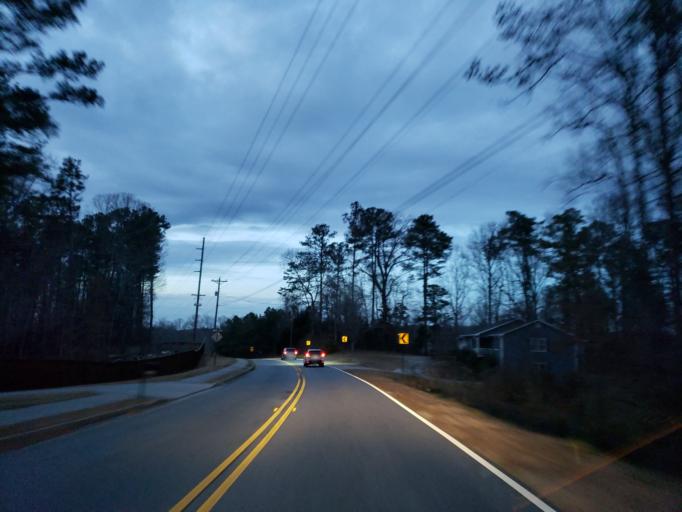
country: US
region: Georgia
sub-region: Cobb County
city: Kennesaw
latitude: 33.9902
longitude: -84.6722
